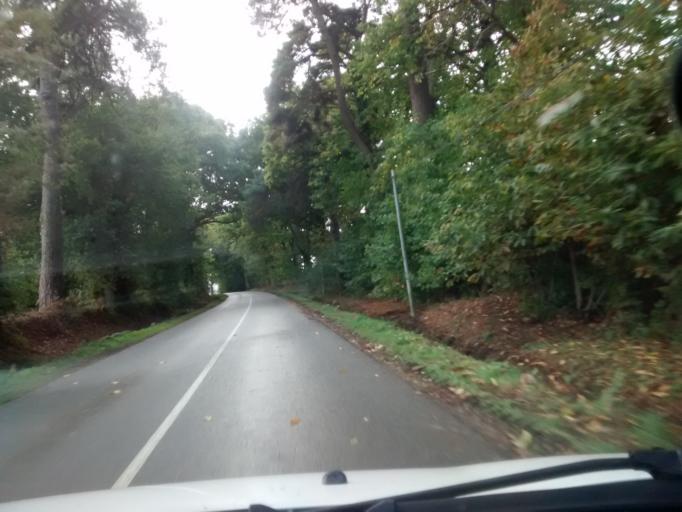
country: FR
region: Brittany
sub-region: Departement d'Ille-et-Vilaine
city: Chateaubourg
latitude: 48.1340
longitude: -1.4076
